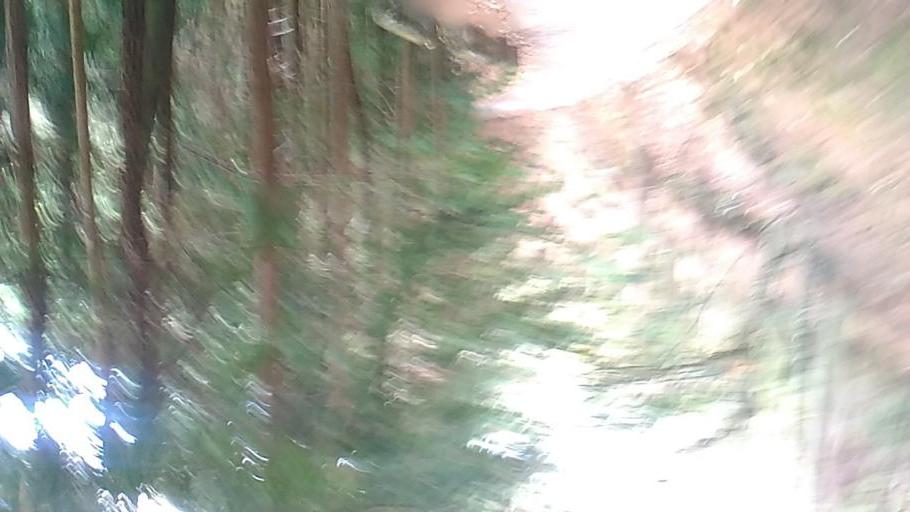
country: TW
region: Taiwan
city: Daxi
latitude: 24.4040
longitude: 121.3055
